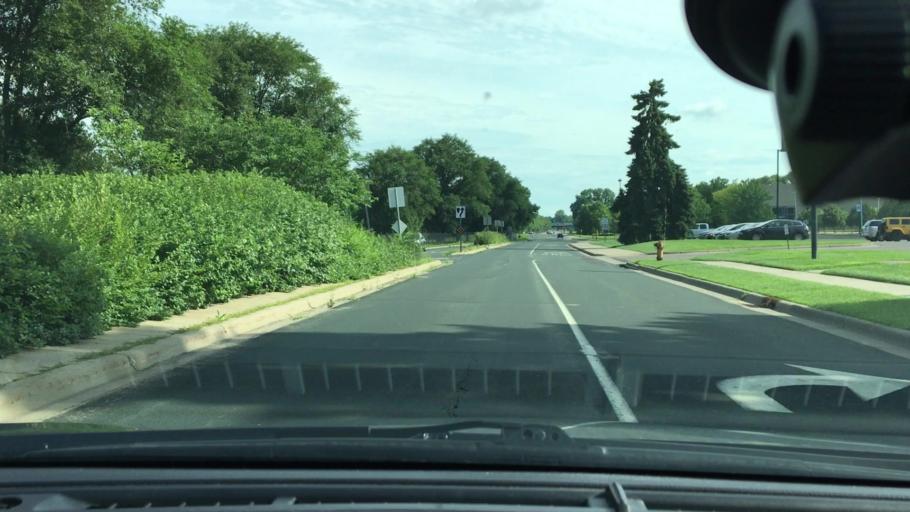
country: US
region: Minnesota
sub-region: Hennepin County
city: Golden Valley
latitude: 44.9831
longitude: -93.3904
